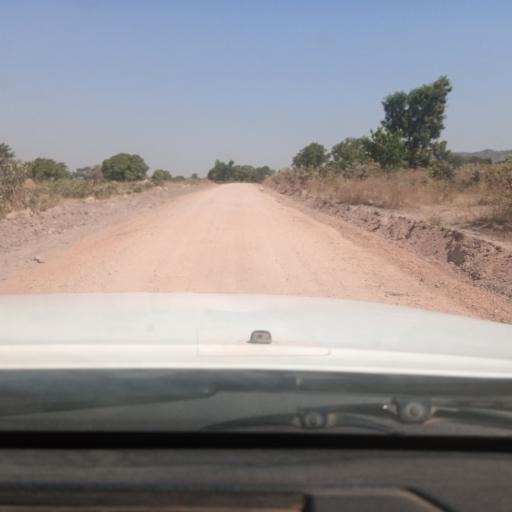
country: NG
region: Adamawa
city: Yola
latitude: 9.0531
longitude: 12.3874
